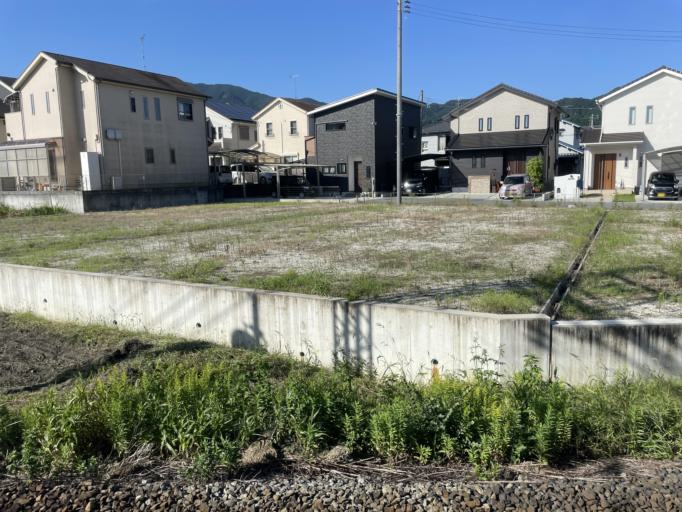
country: JP
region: Nara
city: Gose
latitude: 34.5172
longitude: 135.7054
